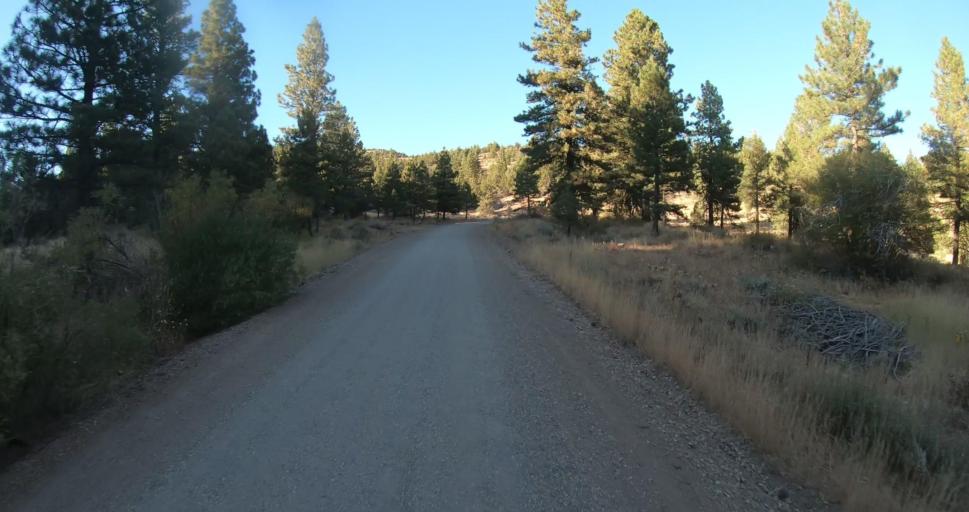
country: US
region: Oregon
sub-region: Lake County
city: Lakeview
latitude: 42.2040
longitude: -120.3006
